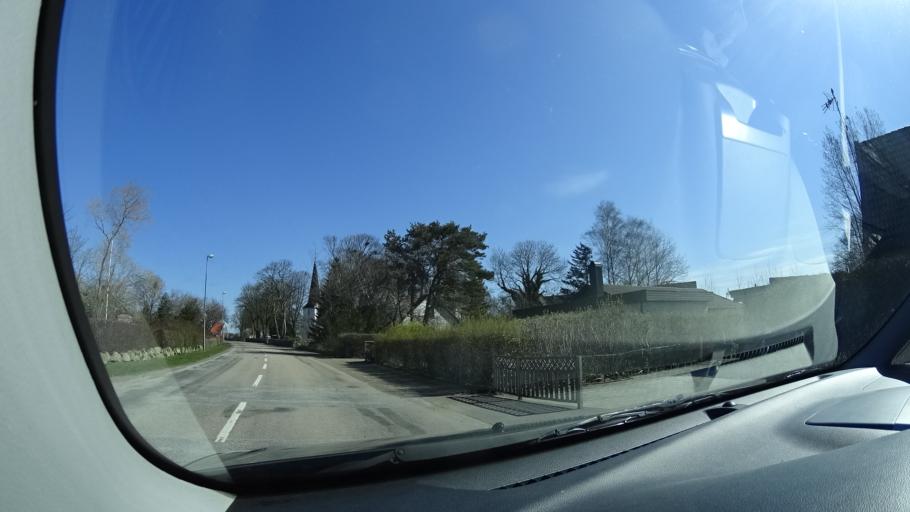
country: SE
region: Skane
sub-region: Hoganas Kommun
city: Hoganas
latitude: 56.2060
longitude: 12.5929
